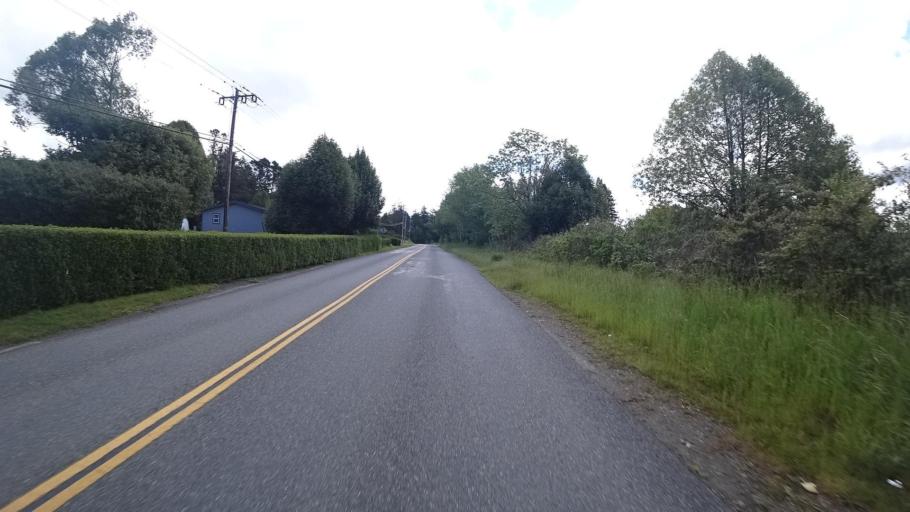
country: US
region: California
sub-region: Humboldt County
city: Blue Lake
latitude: 40.9011
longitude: -124.0275
